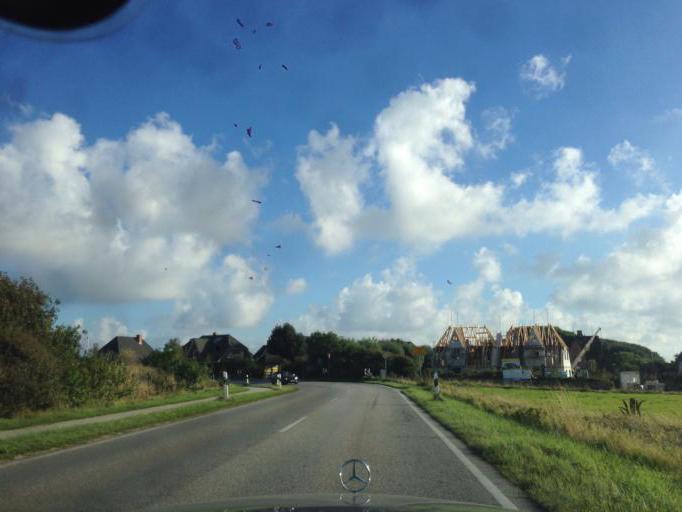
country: DE
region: Schleswig-Holstein
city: Sylt-Ost
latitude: 54.8743
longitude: 8.3921
